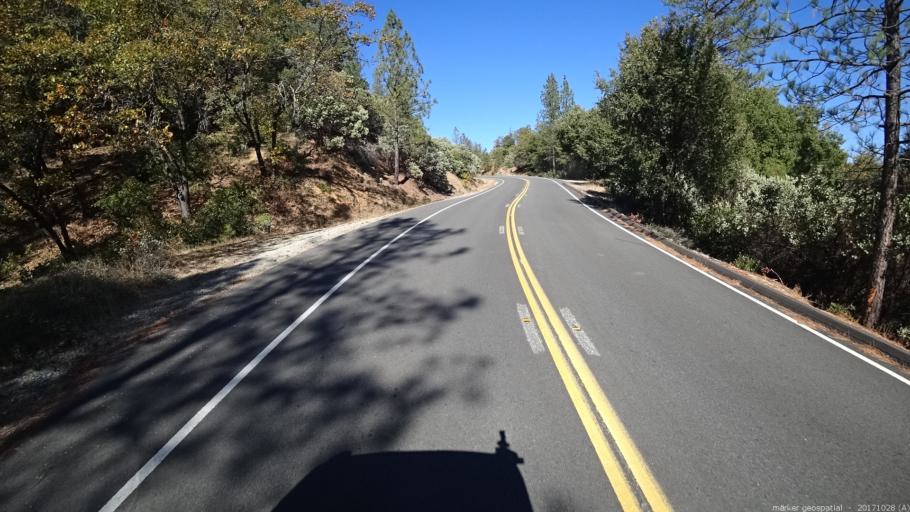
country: US
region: California
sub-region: Shasta County
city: Shasta
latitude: 40.6073
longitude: -122.5588
